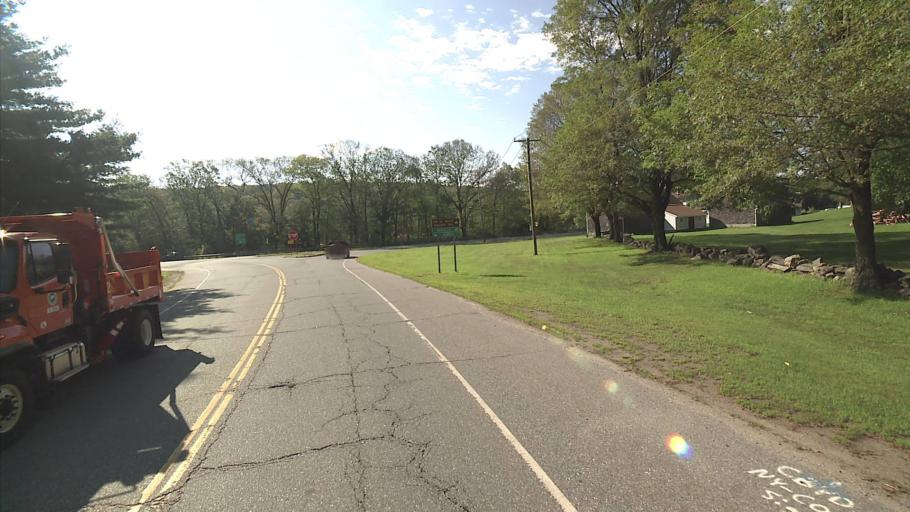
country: US
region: Connecticut
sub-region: New London County
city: Montville Center
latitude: 41.5594
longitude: -72.1637
